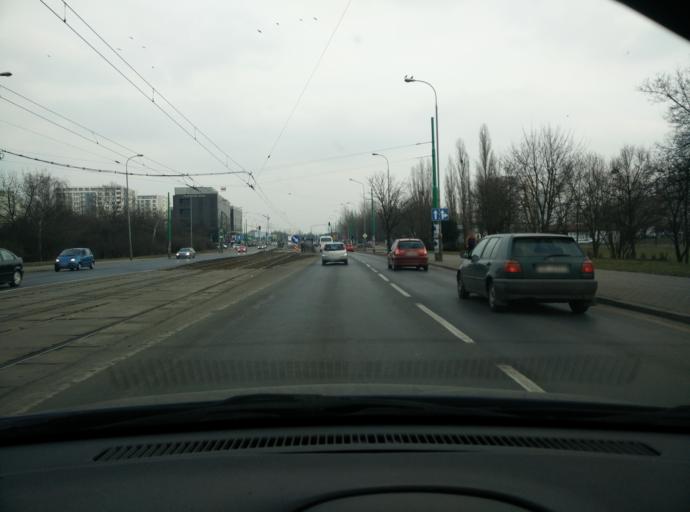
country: PL
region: Greater Poland Voivodeship
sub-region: Poznan
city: Poznan
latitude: 52.3975
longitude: 16.9430
